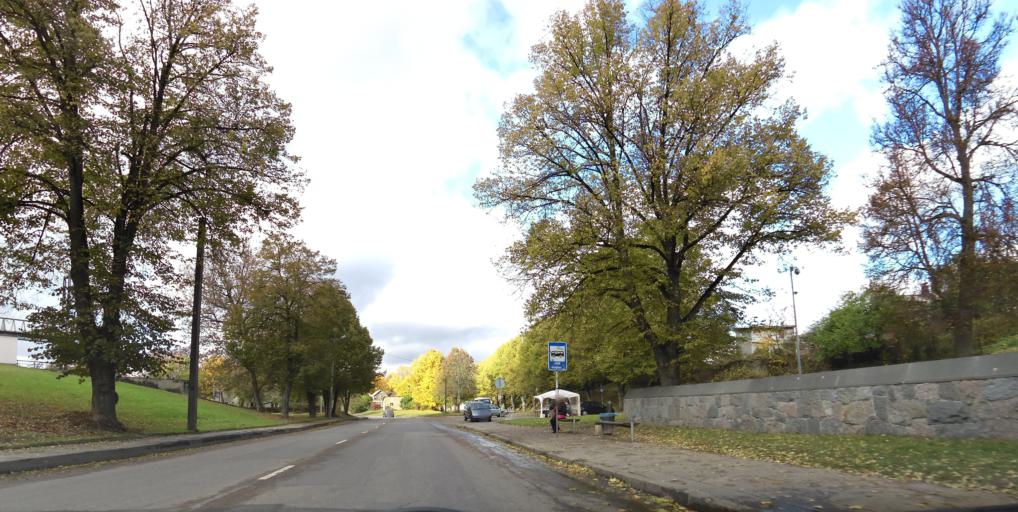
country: LT
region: Vilnius County
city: Rasos
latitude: 54.6704
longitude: 25.3011
